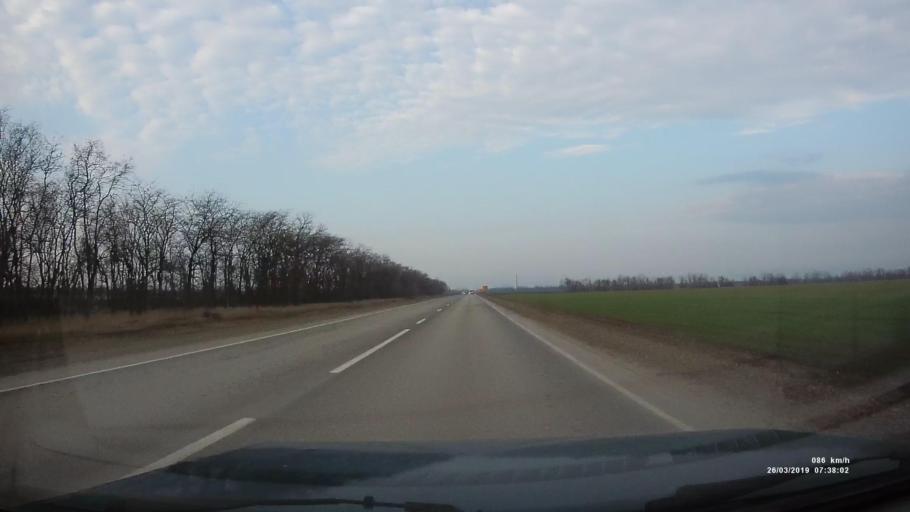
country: RU
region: Rostov
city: Novobessergenovka
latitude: 47.2015
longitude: 38.6896
